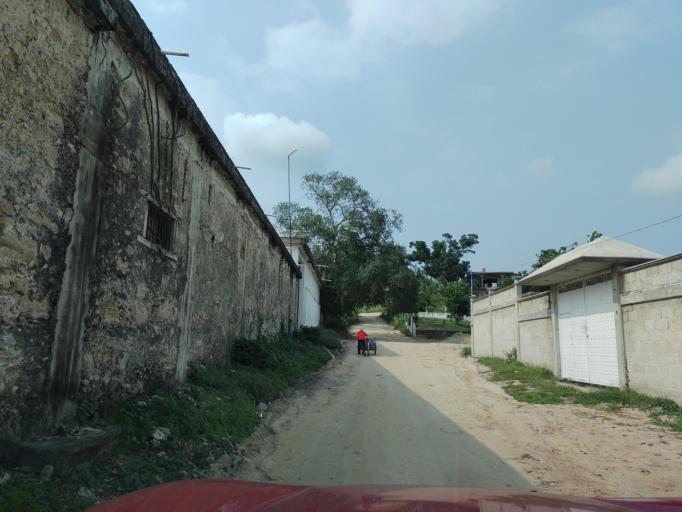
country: MX
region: Veracruz
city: Agua Dulce
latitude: 20.3623
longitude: -97.2953
